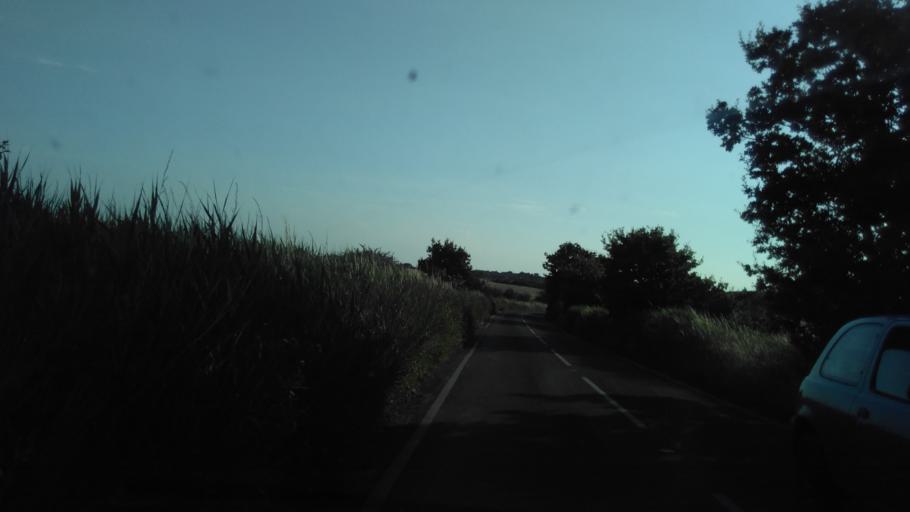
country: GB
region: England
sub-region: Kent
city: Whitstable
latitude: 51.3342
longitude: 0.9976
